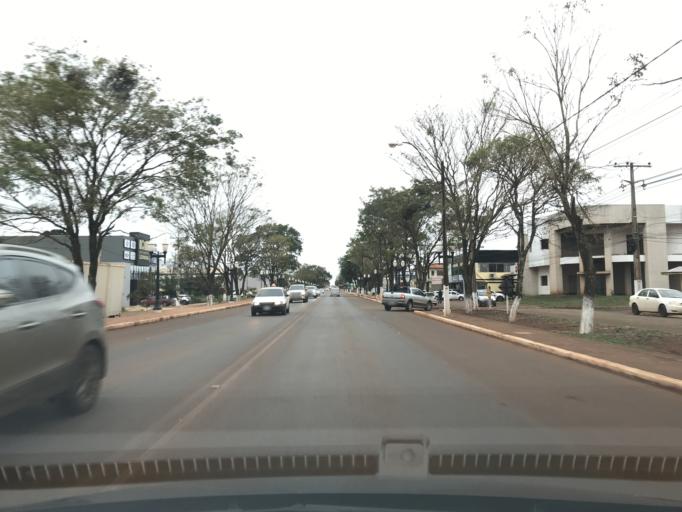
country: PY
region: Canindeyu
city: Colonia Catuete
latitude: -24.2453
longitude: -54.7580
